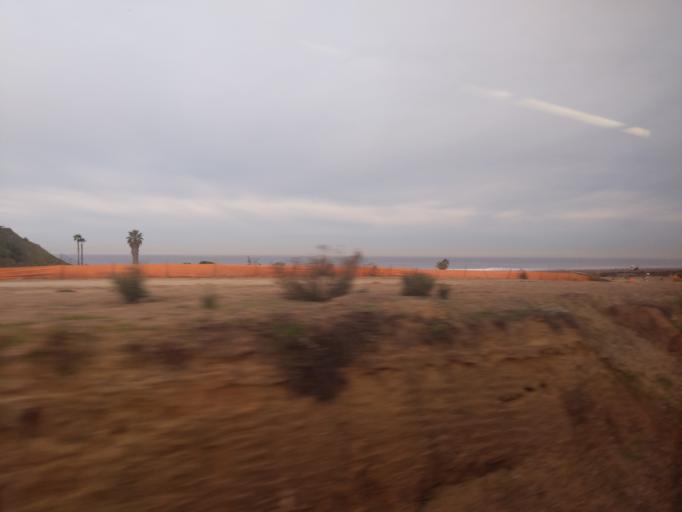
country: US
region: California
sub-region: San Diego County
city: Solana Beach
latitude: 33.0015
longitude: -117.2751
